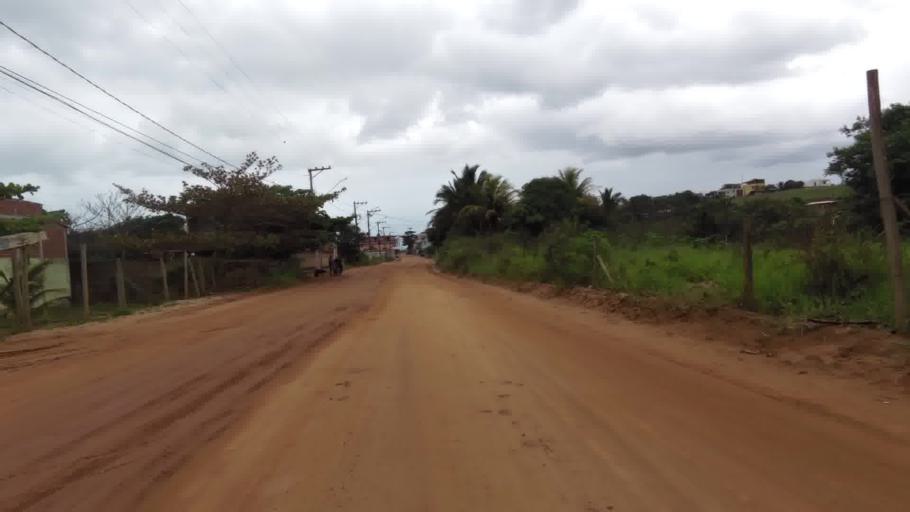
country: BR
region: Espirito Santo
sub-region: Marataizes
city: Marataizes
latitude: -21.0688
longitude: -40.8388
